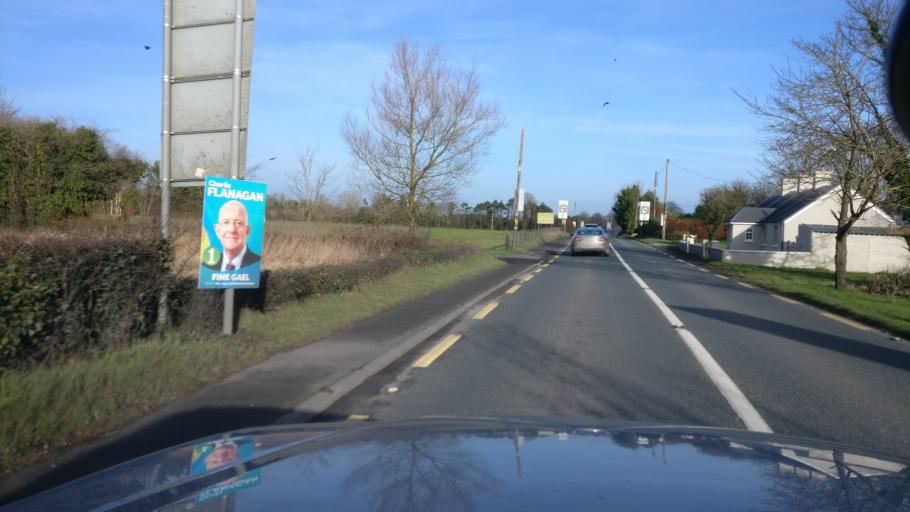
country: IE
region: Leinster
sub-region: Laois
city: Mountmellick
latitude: 53.1034
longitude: -7.3359
